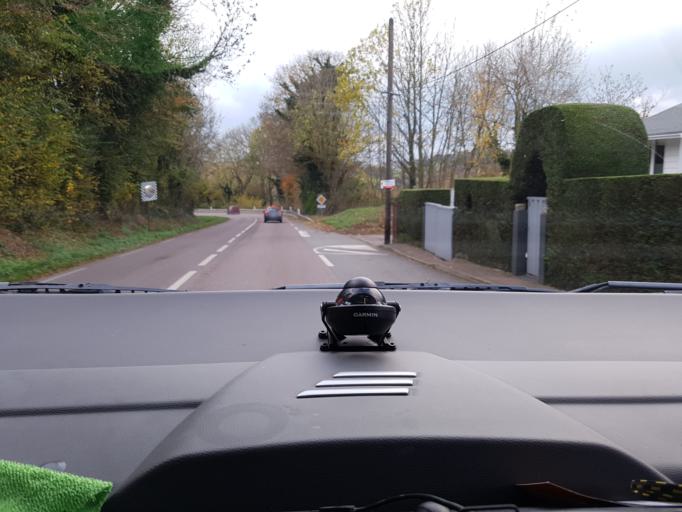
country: FR
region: Haute-Normandie
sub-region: Departement de la Seine-Maritime
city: Rouxmesnil-Bouteilles
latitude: 49.9092
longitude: 1.0623
